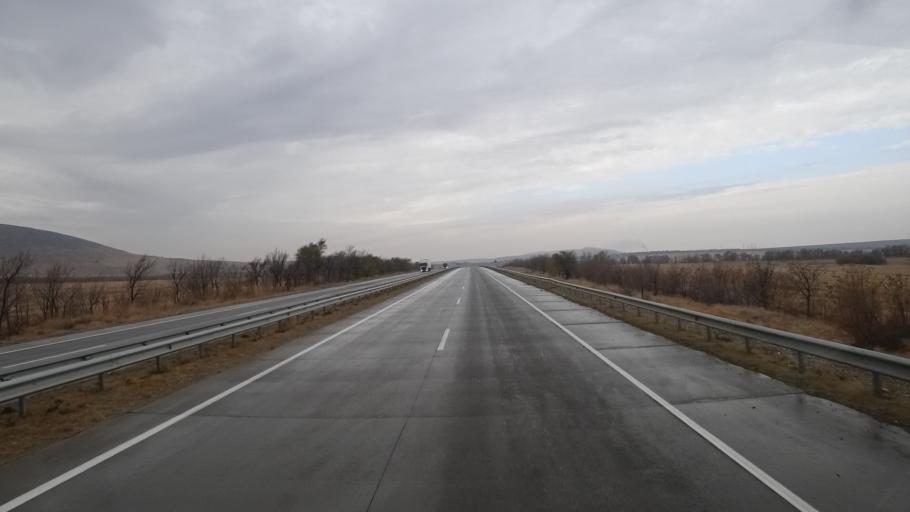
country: KZ
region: Ongtustik Qazaqstan
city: Sastobe
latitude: 42.5439
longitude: 70.0612
